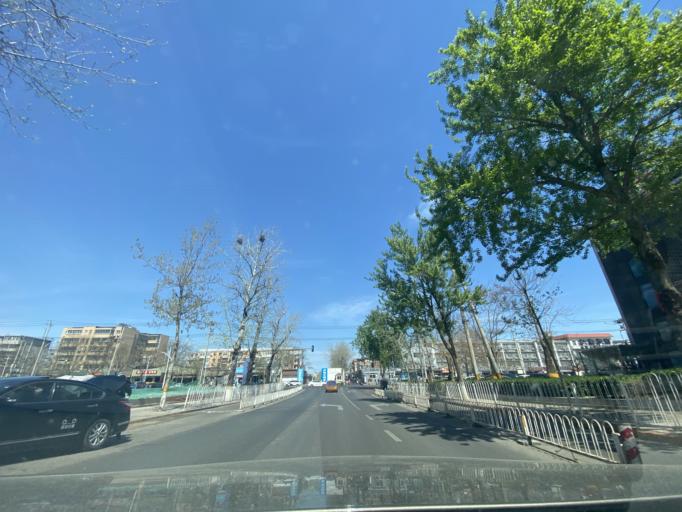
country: CN
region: Beijing
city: Sijiqing
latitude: 39.9271
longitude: 116.2587
